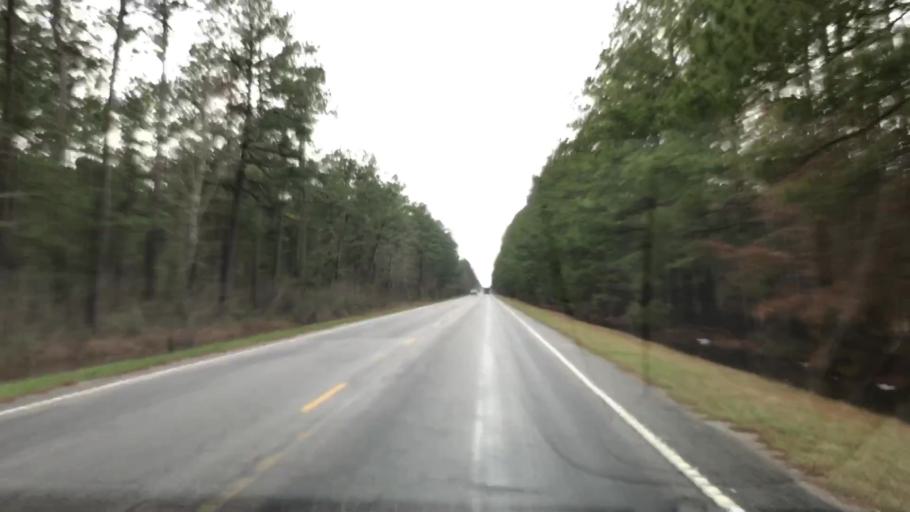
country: US
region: South Carolina
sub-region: Berkeley County
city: Saint Stephen
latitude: 33.2877
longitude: -79.8349
